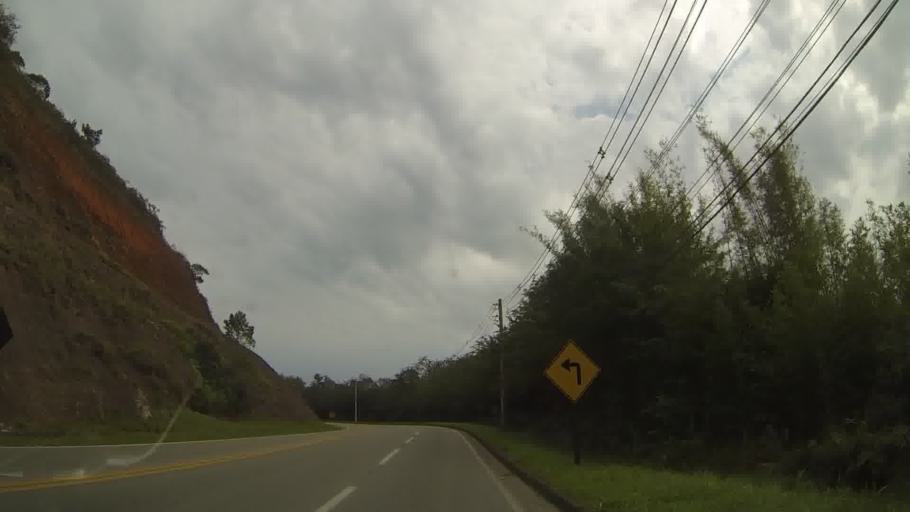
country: BR
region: Sao Paulo
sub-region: Sao Sebastiao
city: Sao Sebastiao
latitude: -23.7946
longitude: -45.5501
